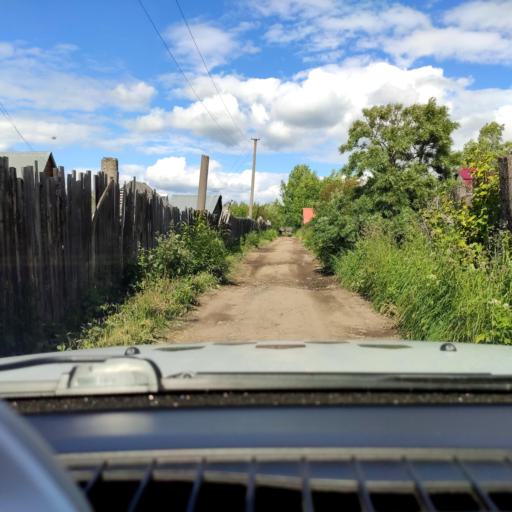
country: RU
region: Perm
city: Overyata
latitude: 58.1030
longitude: 55.8658
